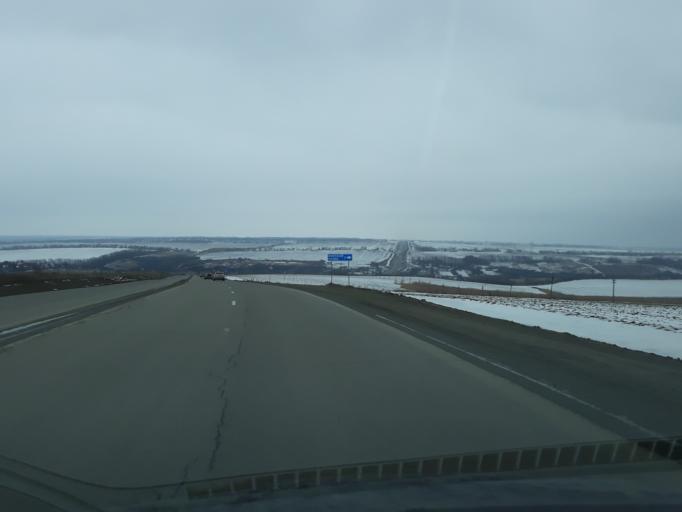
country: RU
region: Rostov
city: Sinyavskoye
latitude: 47.2994
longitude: 39.1973
